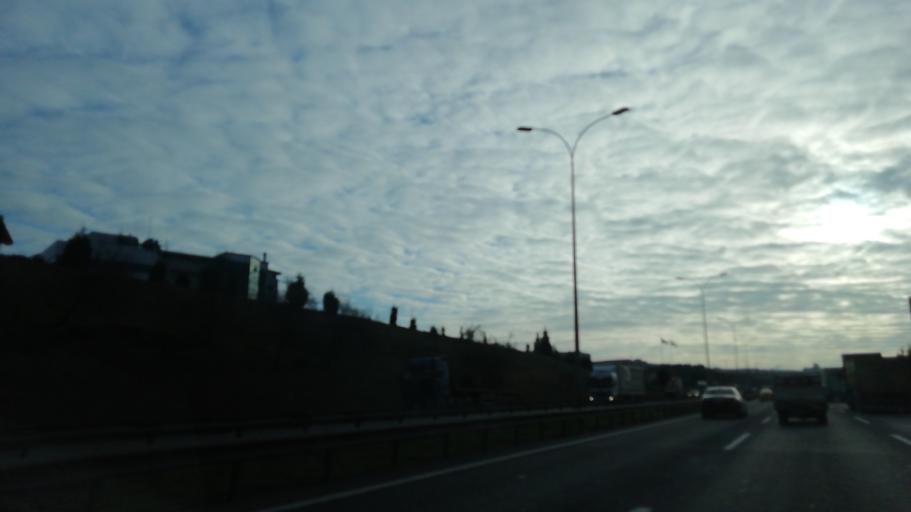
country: TR
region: Kocaeli
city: Balcik
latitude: 40.8782
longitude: 29.3848
